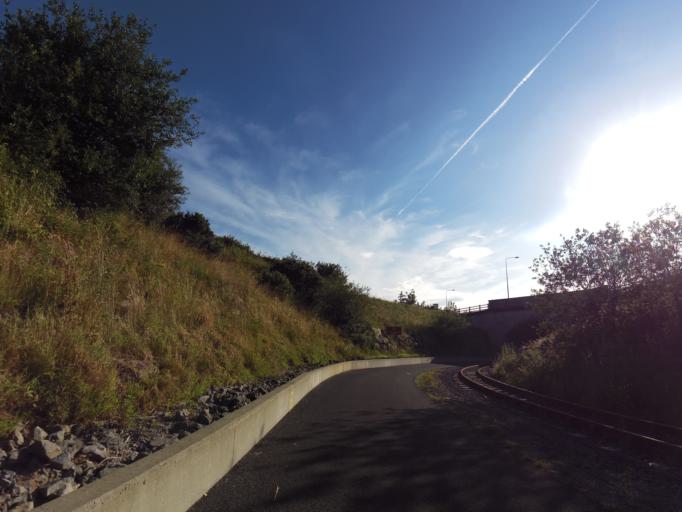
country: IE
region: Munster
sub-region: Waterford
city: Waterford
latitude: 52.2694
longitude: -7.1680
